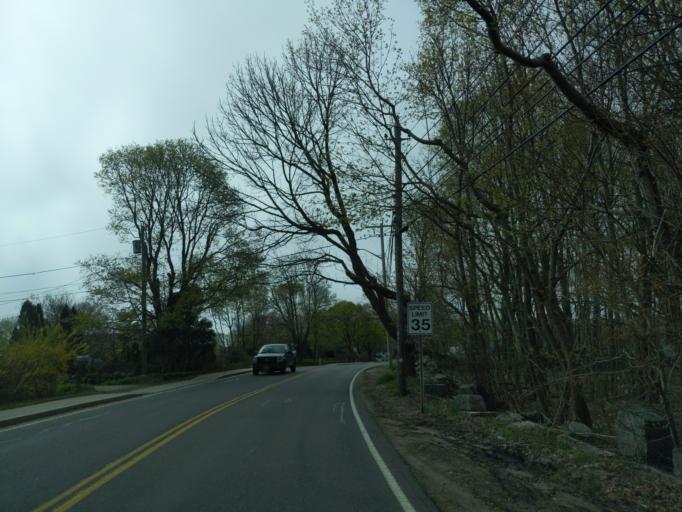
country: US
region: Massachusetts
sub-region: Essex County
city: Rockport
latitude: 42.6525
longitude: -70.6007
